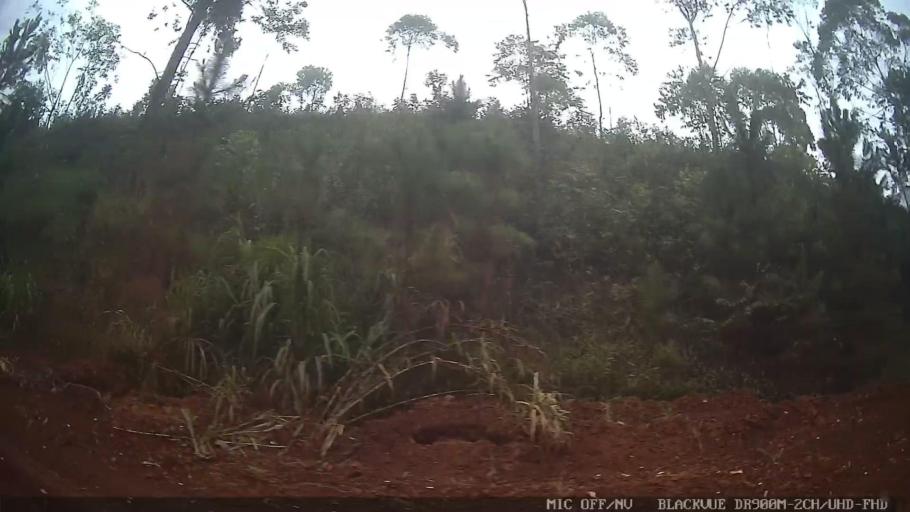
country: BR
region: Sao Paulo
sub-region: Suzano
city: Suzano
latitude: -23.6512
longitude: -46.2609
